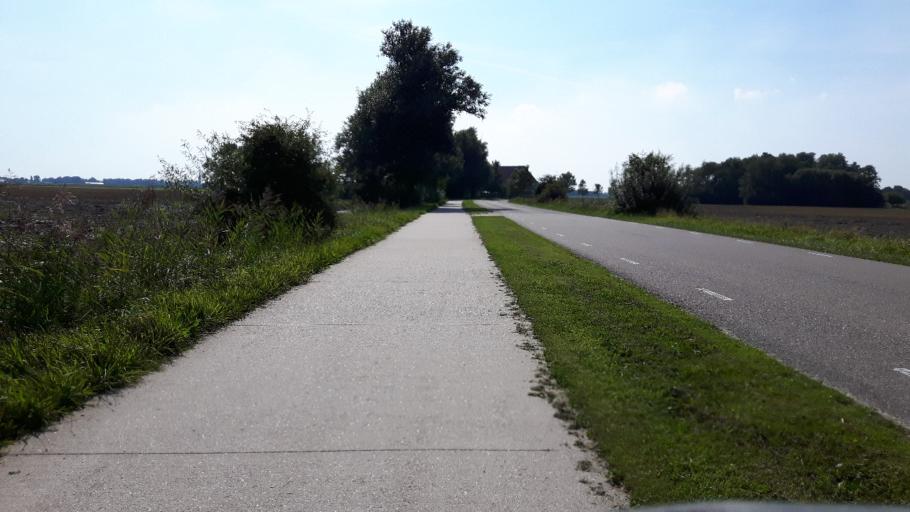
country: NL
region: Friesland
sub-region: Gemeente Franekeradeel
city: Tzummarum
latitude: 53.2108
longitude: 5.5578
